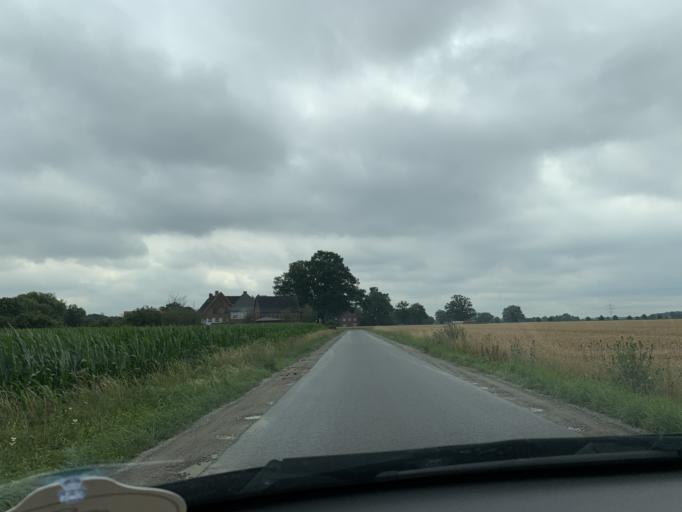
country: DE
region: North Rhine-Westphalia
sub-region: Regierungsbezirk Munster
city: Ennigerloh
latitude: 51.8516
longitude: 8.0825
